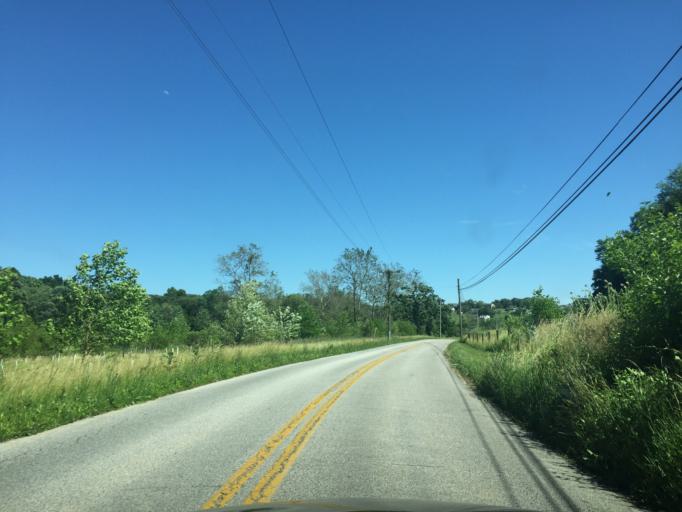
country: US
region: Maryland
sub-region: Carroll County
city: Hampstead
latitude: 39.6145
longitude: -76.8853
